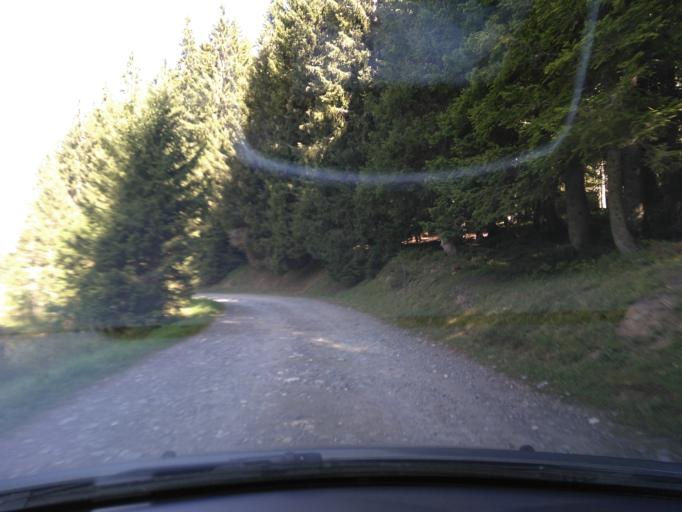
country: FR
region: Rhone-Alpes
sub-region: Departement de la Haute-Savoie
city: Praz-sur-Arly
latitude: 45.7824
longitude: 6.5259
